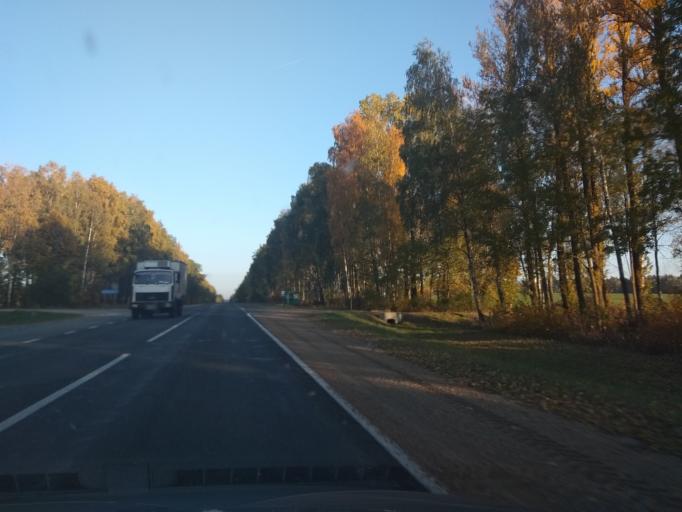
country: BY
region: Grodnenskaya
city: Vawkavysk
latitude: 53.1498
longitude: 24.5653
